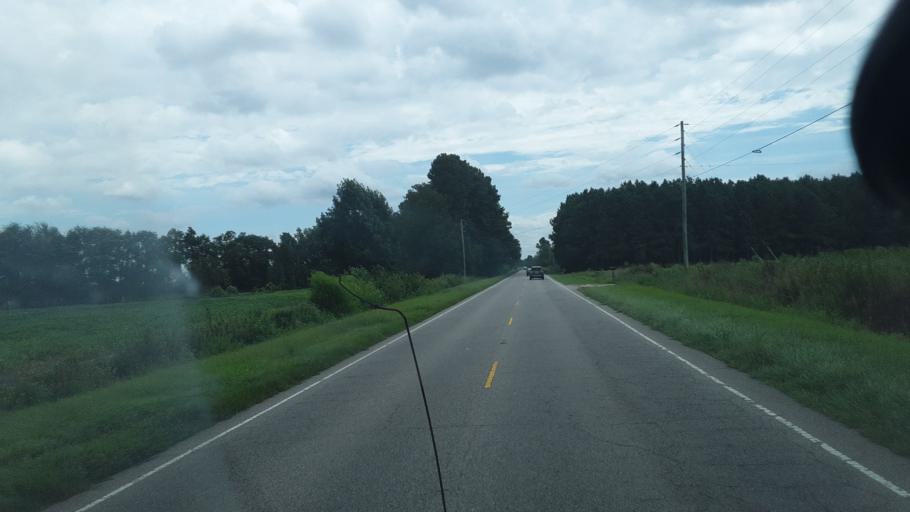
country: US
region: North Carolina
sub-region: Robeson County
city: Maxton
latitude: 34.6622
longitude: -79.3908
